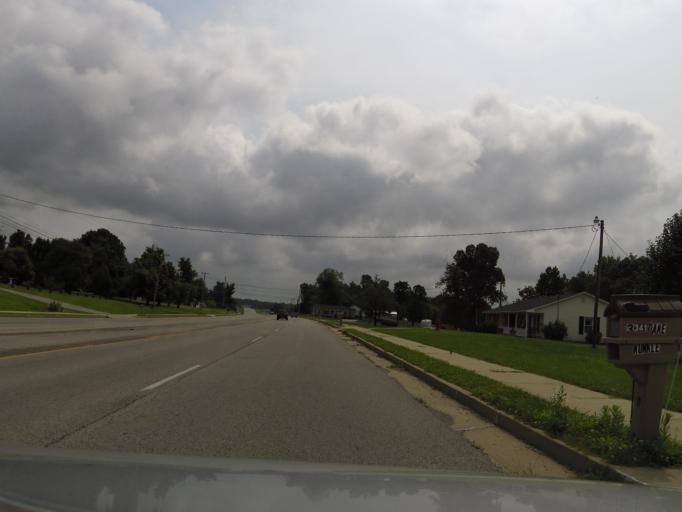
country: US
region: Kentucky
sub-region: Hopkins County
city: Madisonville
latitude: 37.3290
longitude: -87.4377
